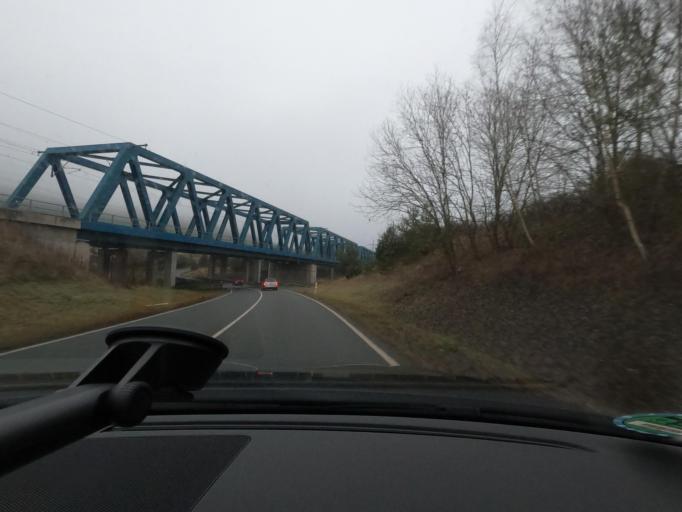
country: DE
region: Thuringia
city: Behringen
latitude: 50.7660
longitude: 11.0023
